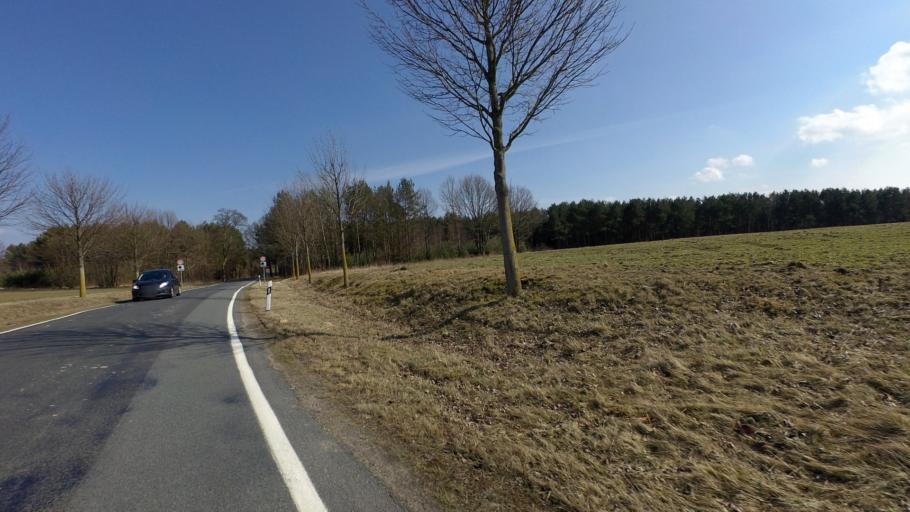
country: DE
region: Brandenburg
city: Wiesenburg
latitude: 52.0860
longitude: 12.4605
